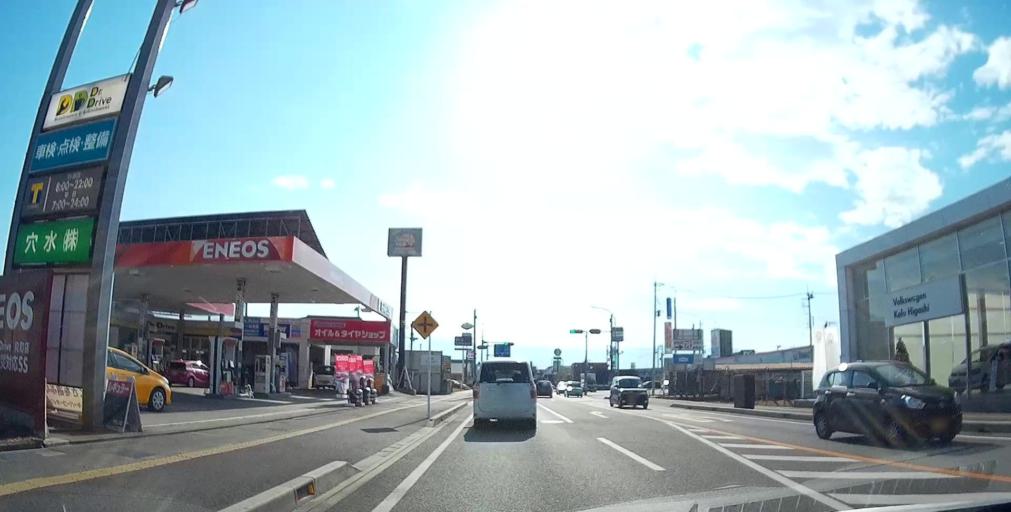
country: JP
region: Yamanashi
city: Isawa
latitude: 35.6497
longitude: 138.6130
